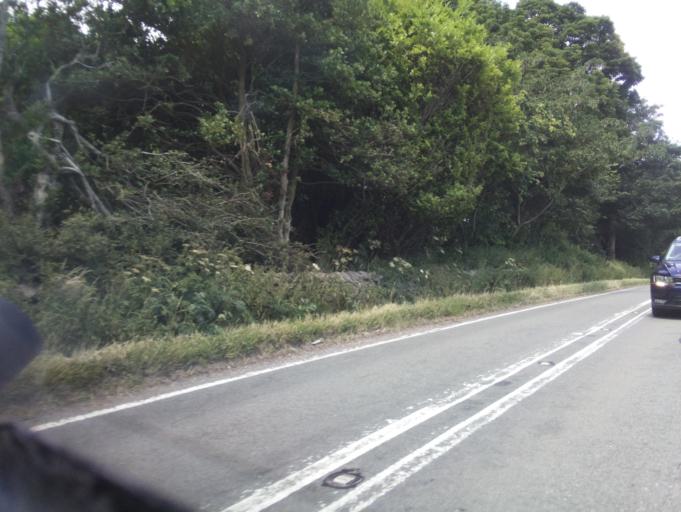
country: GB
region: England
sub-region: Derbyshire
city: Ashbourne
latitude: 53.0967
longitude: -1.7732
